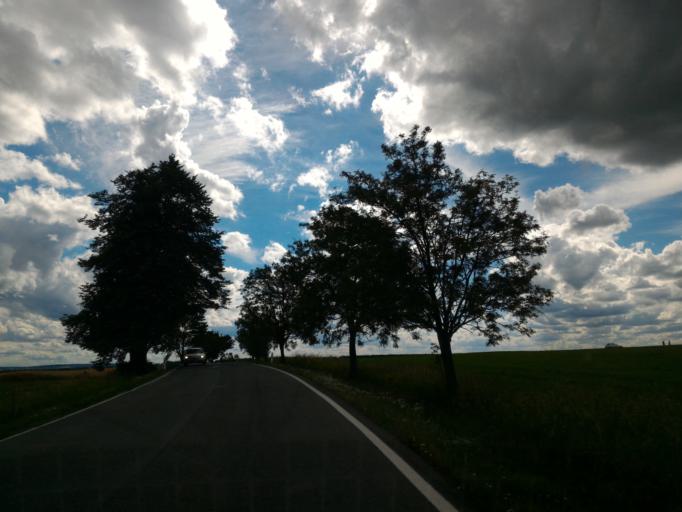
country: CZ
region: Vysocina
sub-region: Okres Jihlava
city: Polna
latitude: 49.4379
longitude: 15.7308
